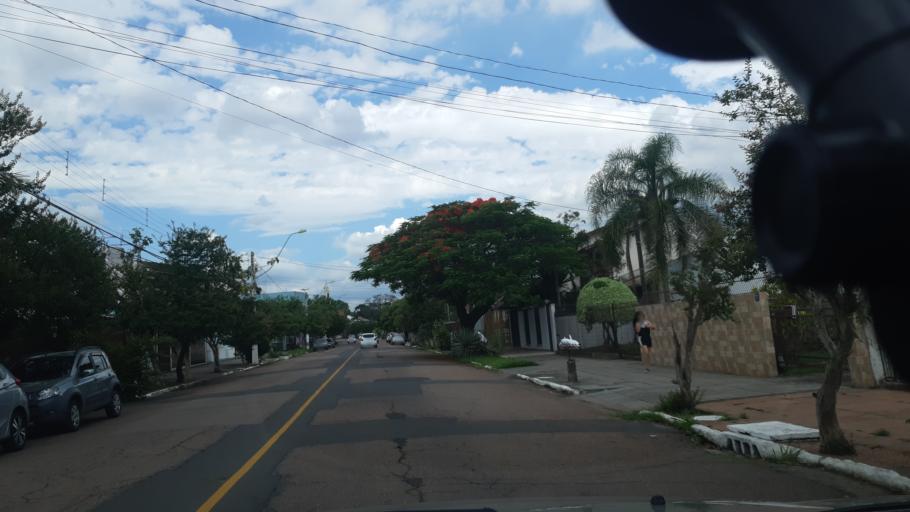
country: BR
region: Rio Grande do Sul
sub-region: Esteio
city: Esteio
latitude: -29.8502
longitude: -51.1701
